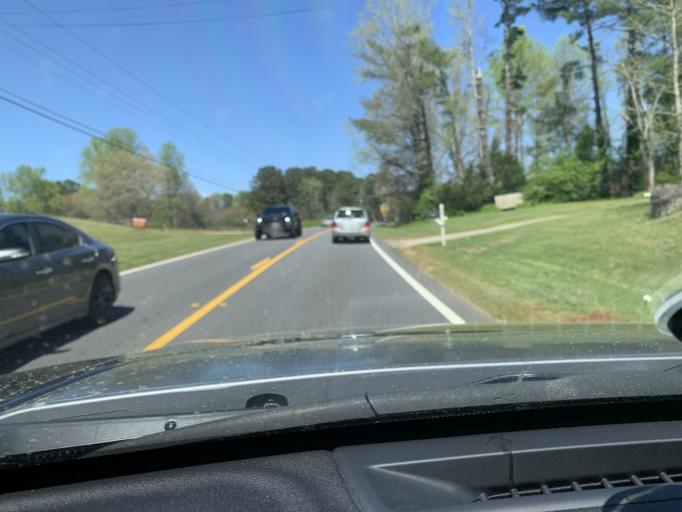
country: US
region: Georgia
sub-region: Fulton County
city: Milton
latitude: 34.1650
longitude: -84.2356
